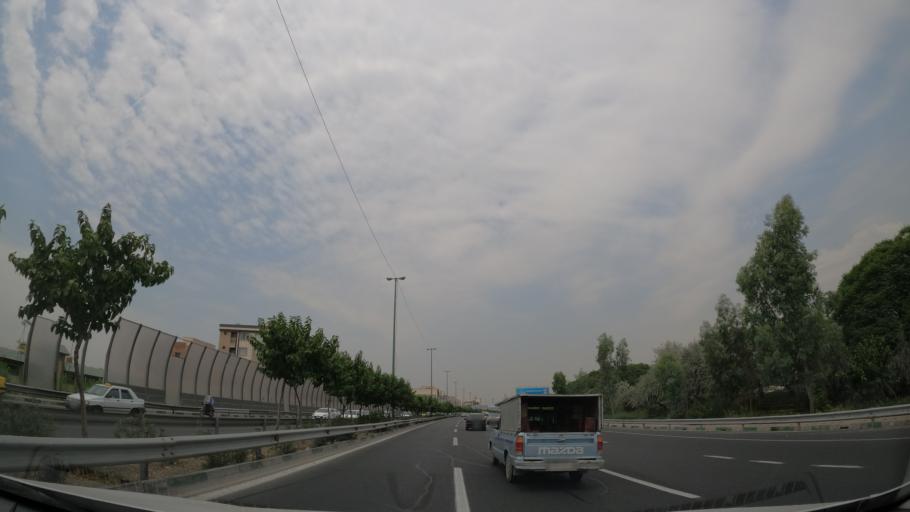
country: IR
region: Tehran
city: Tehran
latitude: 35.7389
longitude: 51.3622
